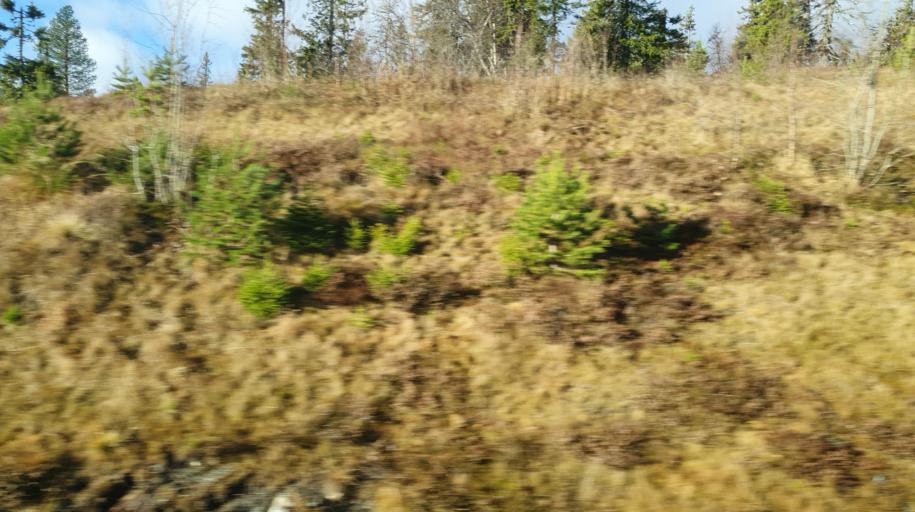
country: NO
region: Buskerud
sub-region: Krodsherad
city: Noresund
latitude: 60.2255
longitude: 9.5199
